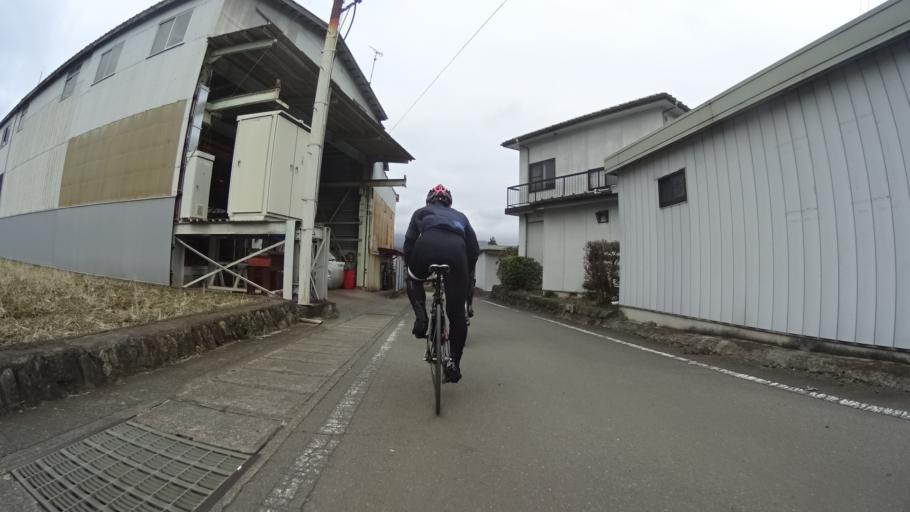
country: JP
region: Yamanashi
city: Otsuki
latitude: 35.5865
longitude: 138.9297
